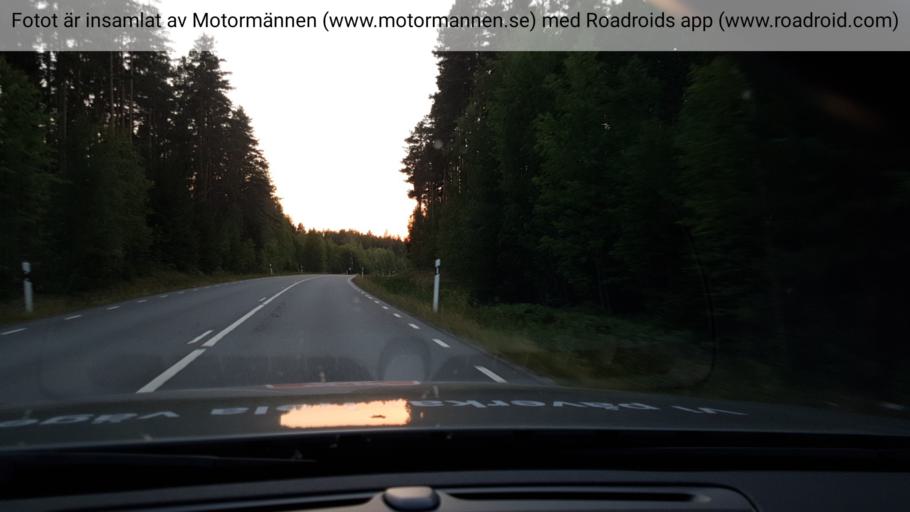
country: SE
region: Uppsala
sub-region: Heby Kommun
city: OEstervala
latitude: 60.1439
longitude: 17.2067
